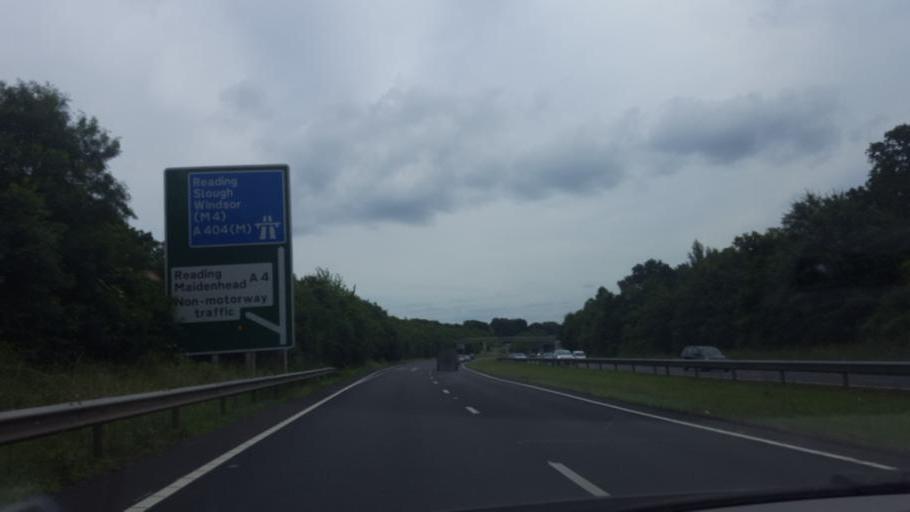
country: GB
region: England
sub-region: Royal Borough of Windsor and Maidenhead
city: Bisham
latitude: 51.5226
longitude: -0.7683
